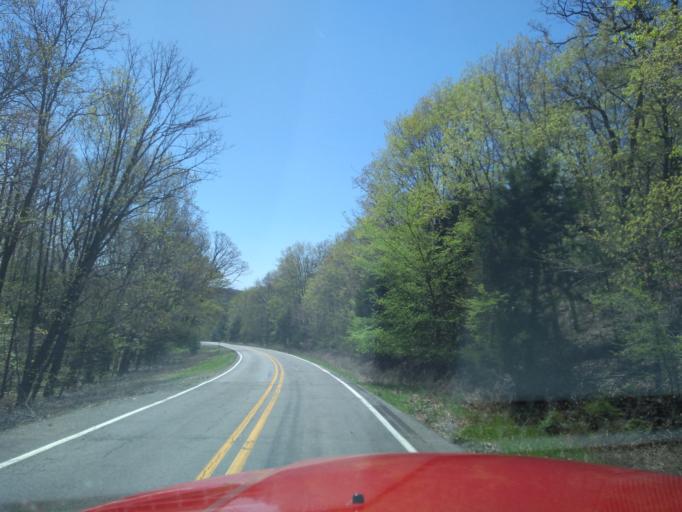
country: US
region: Arkansas
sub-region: Washington County
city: West Fork
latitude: 35.7831
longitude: -94.2580
